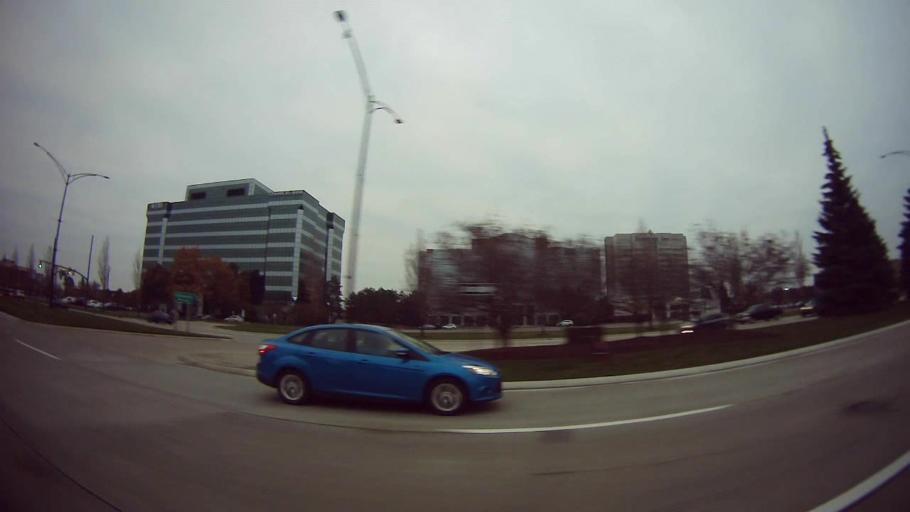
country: US
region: Michigan
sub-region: Oakland County
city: Birmingham
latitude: 42.5616
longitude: -83.1793
